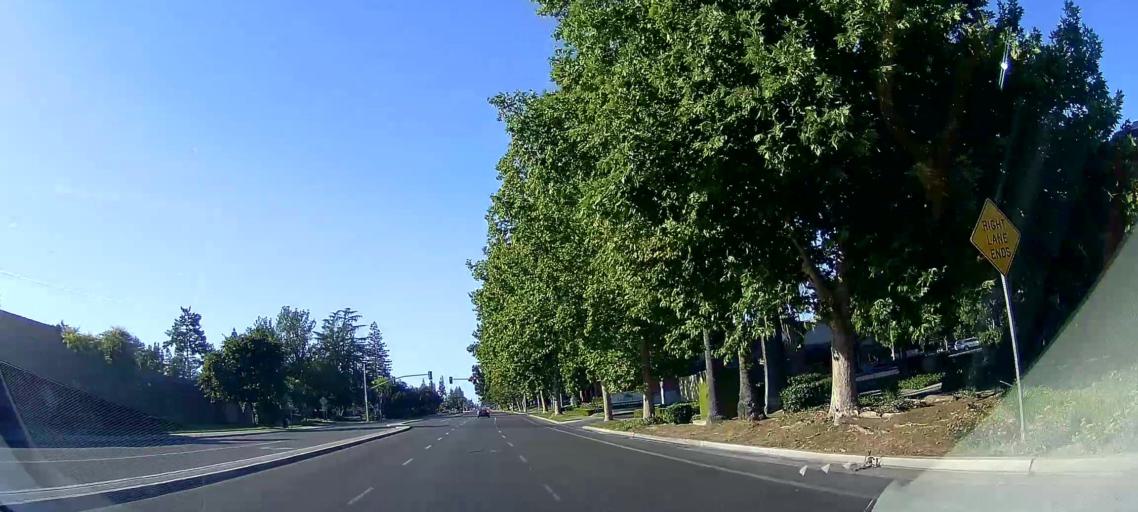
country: US
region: California
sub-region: Fresno County
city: Fresno
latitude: 36.8109
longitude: -119.8084
